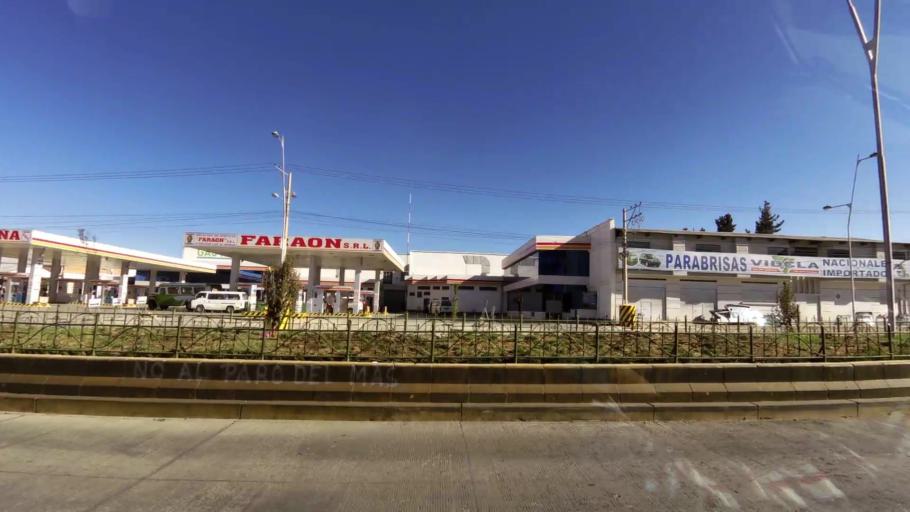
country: BO
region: La Paz
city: La Paz
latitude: -16.5227
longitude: -68.1797
